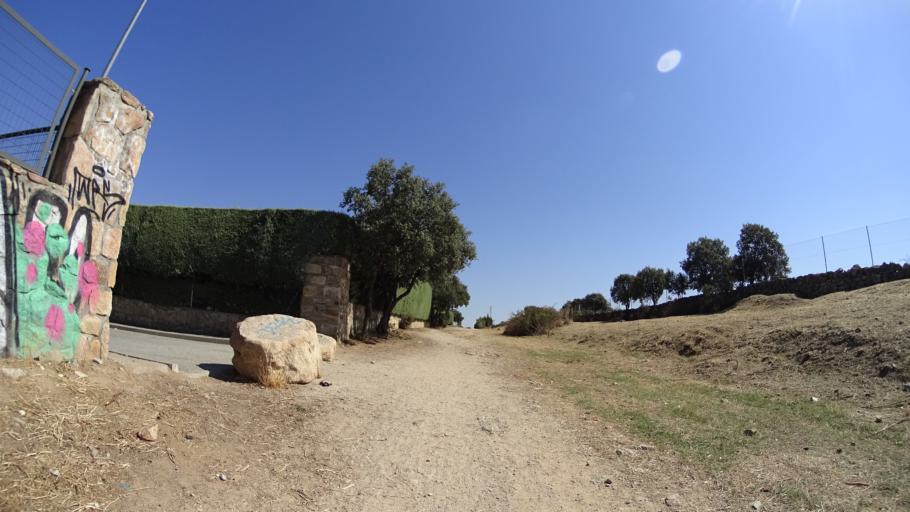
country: ES
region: Madrid
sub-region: Provincia de Madrid
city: Collado-Villalba
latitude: 40.6131
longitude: -4.0133
